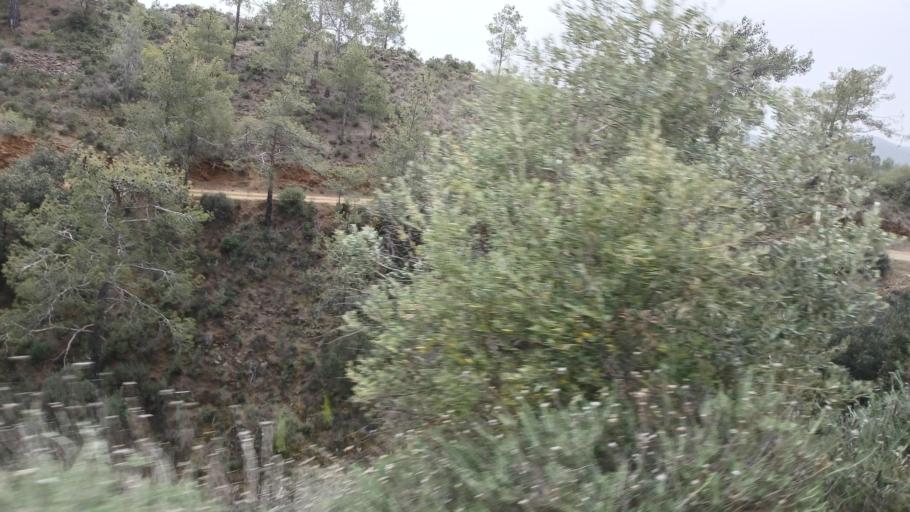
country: CY
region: Limassol
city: Parekklisha
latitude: 34.8547
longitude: 33.1080
